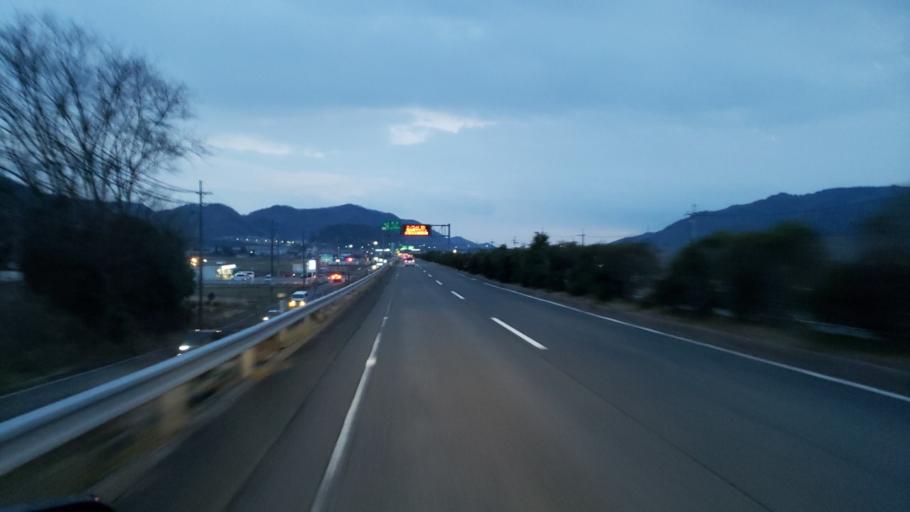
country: JP
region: Hyogo
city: Himeji
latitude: 34.8843
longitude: 134.7430
